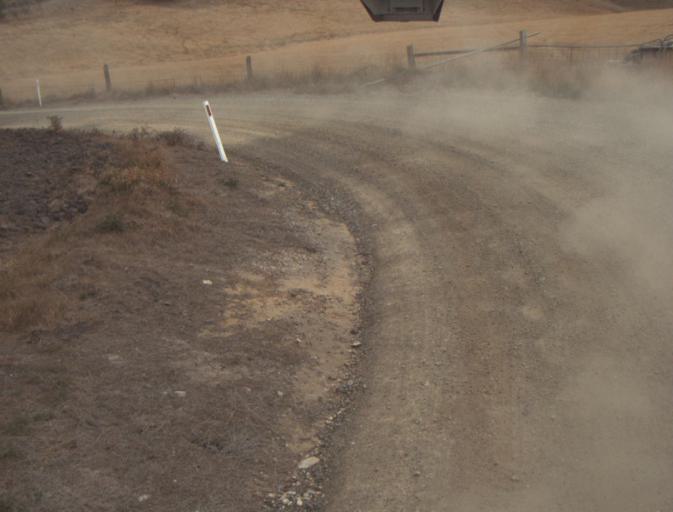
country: AU
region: Tasmania
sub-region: Launceston
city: Mayfield
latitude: -41.1648
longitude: 147.2124
